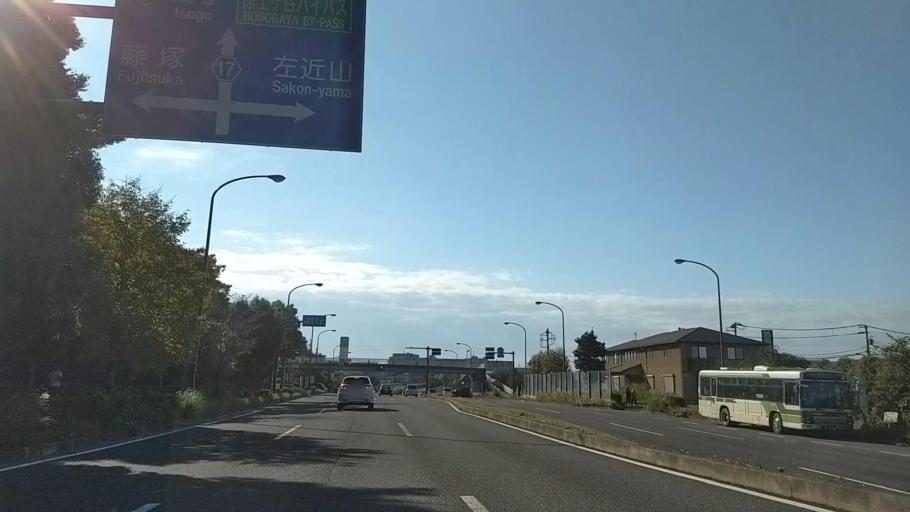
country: JP
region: Kanagawa
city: Yokohama
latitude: 35.4584
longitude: 139.5630
